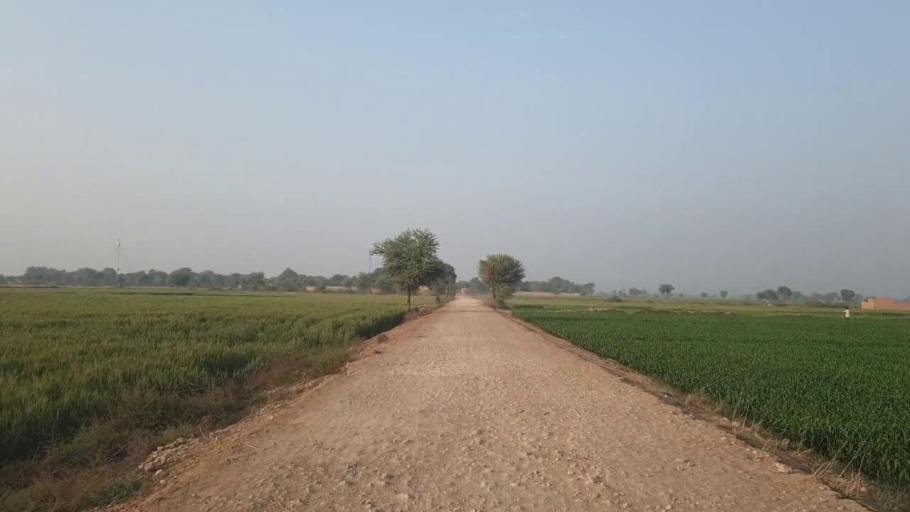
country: PK
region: Sindh
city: Bhit Shah
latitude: 25.8094
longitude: 68.4769
